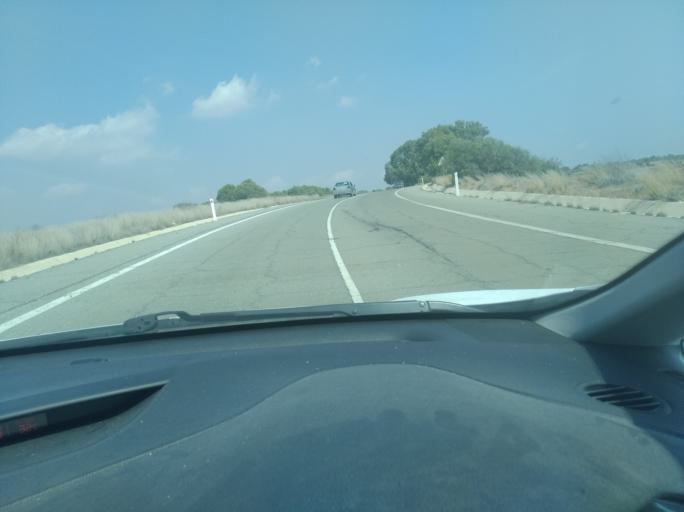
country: CY
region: Larnaka
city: Xylotymbou
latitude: 34.9817
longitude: 33.7828
